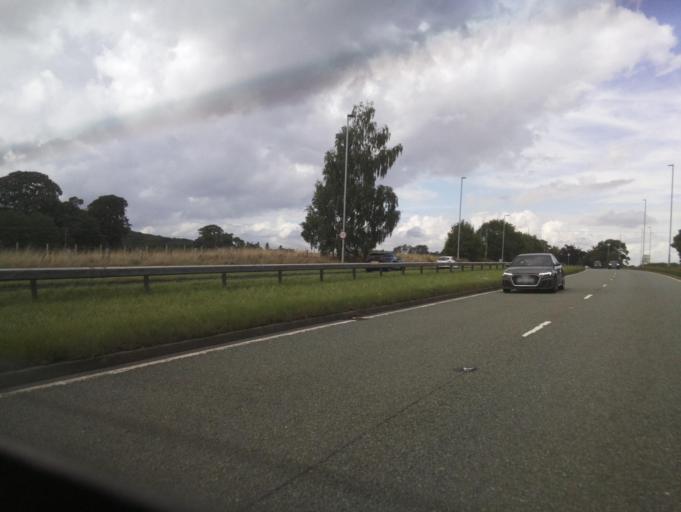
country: GB
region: England
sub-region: Staffordshire
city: Barlaston
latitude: 52.9538
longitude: -2.1920
